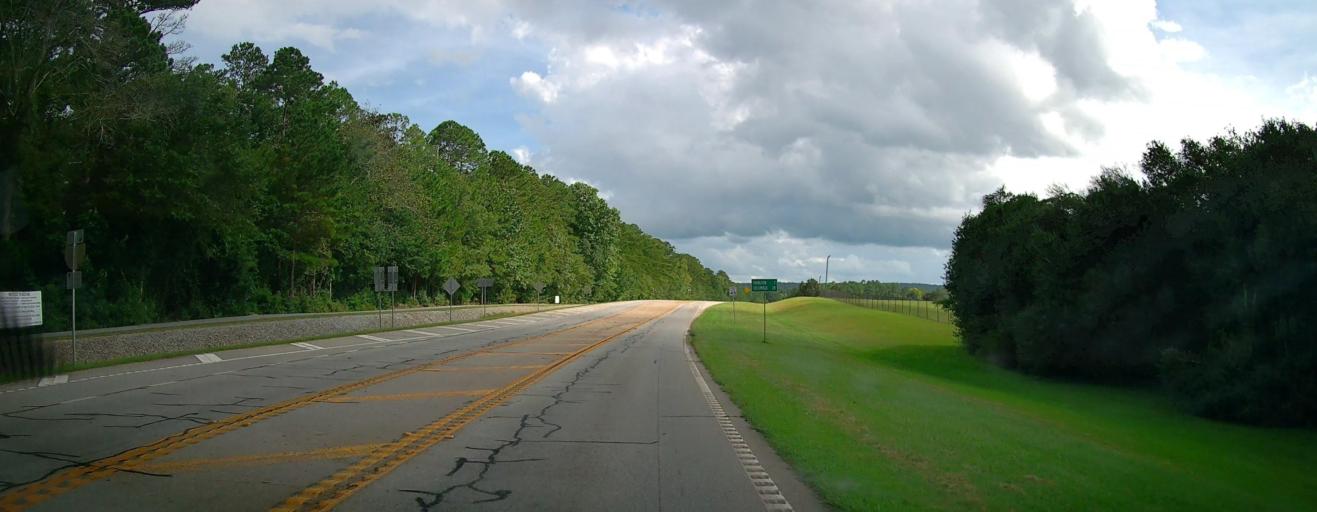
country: US
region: Georgia
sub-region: Harris County
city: Pine Mountain
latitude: 32.8518
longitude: -84.8463
